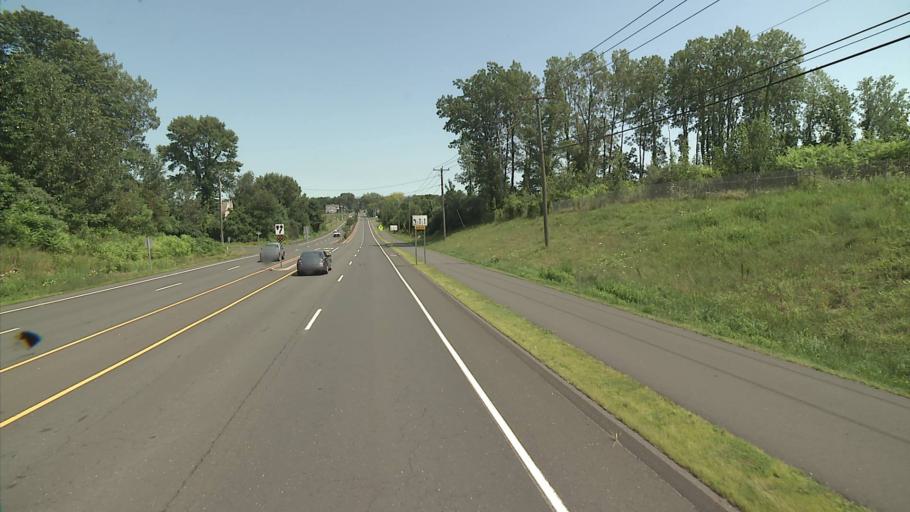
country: US
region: Connecticut
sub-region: Hartford County
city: Tariffville
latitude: 41.9445
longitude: -72.7342
